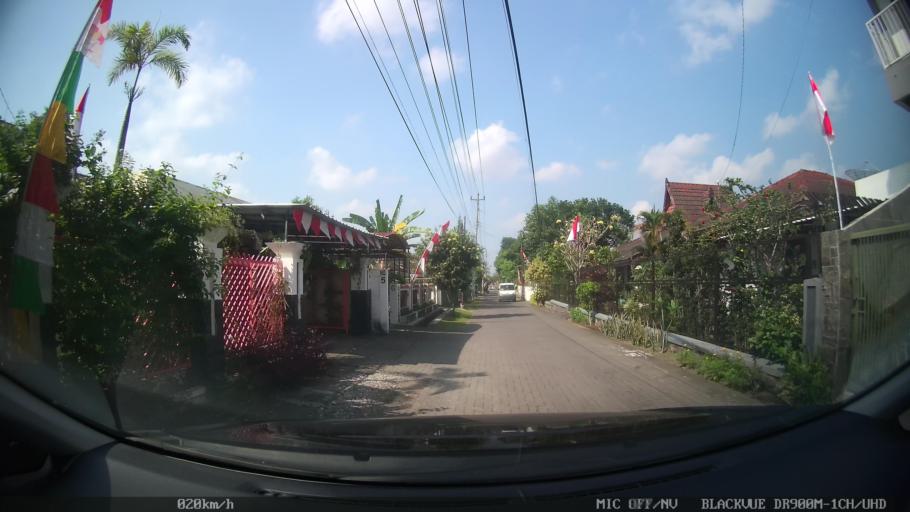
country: ID
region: Daerah Istimewa Yogyakarta
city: Melati
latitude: -7.7569
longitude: 110.3908
